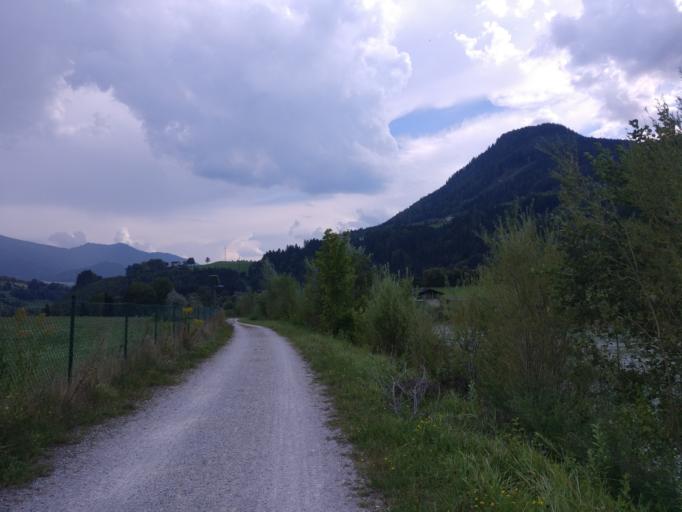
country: AT
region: Salzburg
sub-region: Politischer Bezirk Sankt Johann im Pongau
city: Pfarrwerfen
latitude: 47.4588
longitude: 13.2003
